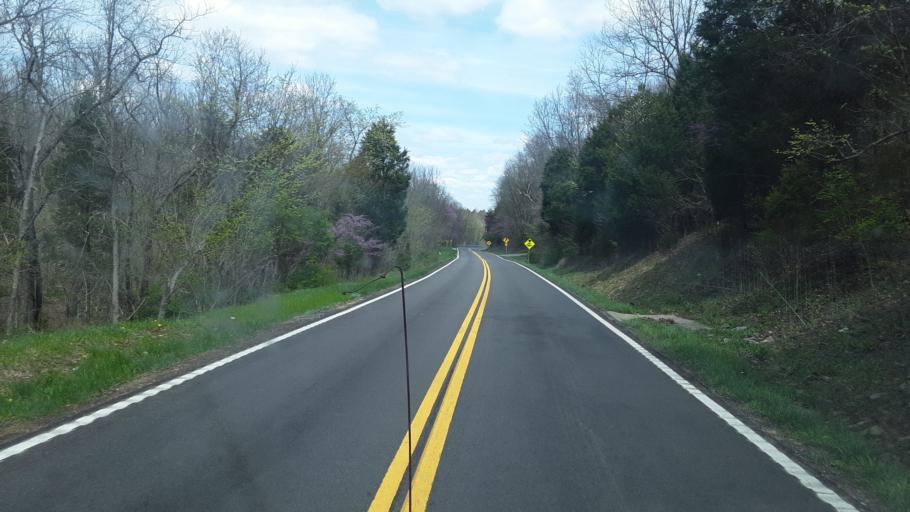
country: US
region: Kentucky
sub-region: Grant County
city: Dry Ridge
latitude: 38.6550
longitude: -84.6772
